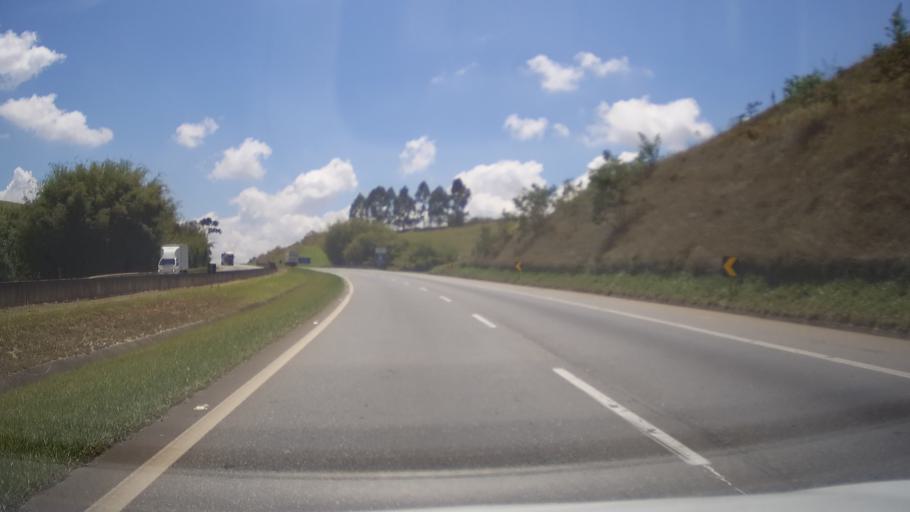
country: BR
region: Minas Gerais
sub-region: Sao Goncalo Do Sapucai
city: Sao Goncalo do Sapucai
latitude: -21.9083
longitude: -45.5613
